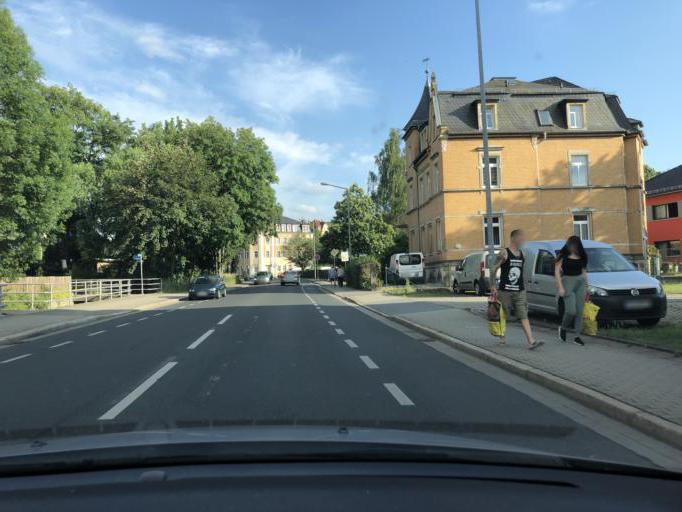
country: DE
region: Saxony
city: Freital
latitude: 50.9951
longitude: 13.6537
